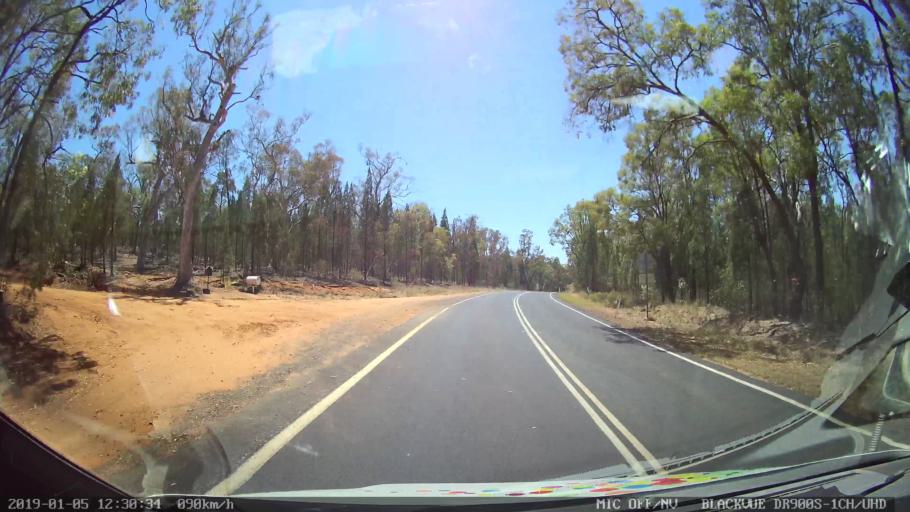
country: AU
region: New South Wales
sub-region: Warrumbungle Shire
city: Coonabarabran
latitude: -31.2267
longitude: 149.3519
